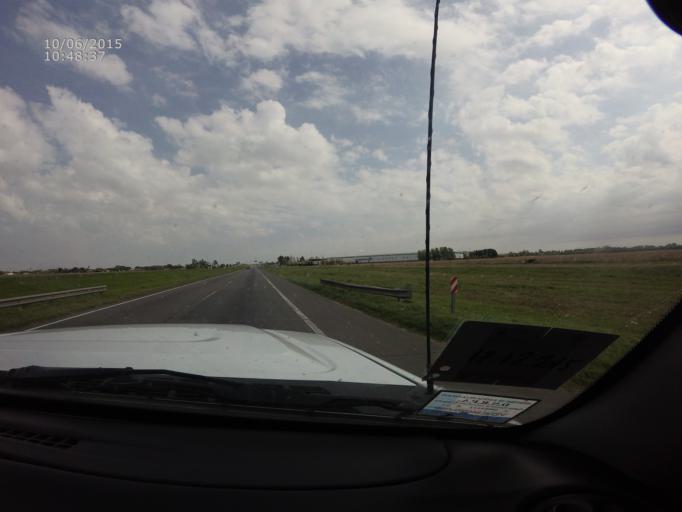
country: AR
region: Buenos Aires
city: San Nicolas de los Arroyos
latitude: -33.3939
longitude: -60.2135
